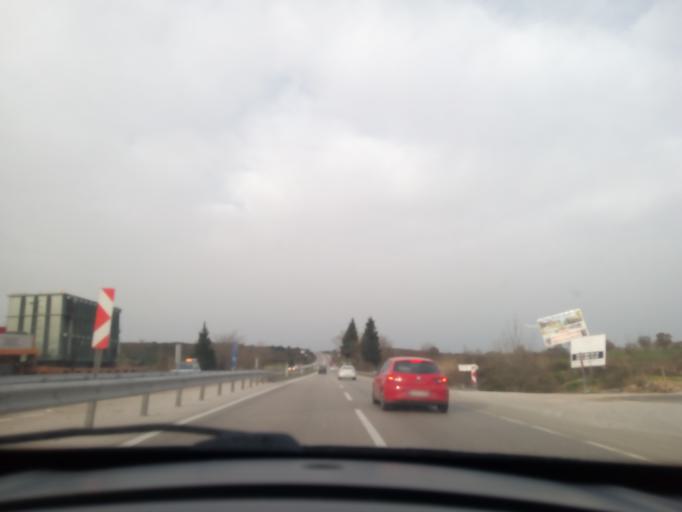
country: TR
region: Bursa
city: Mahmudiye
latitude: 40.2164
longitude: 28.6535
